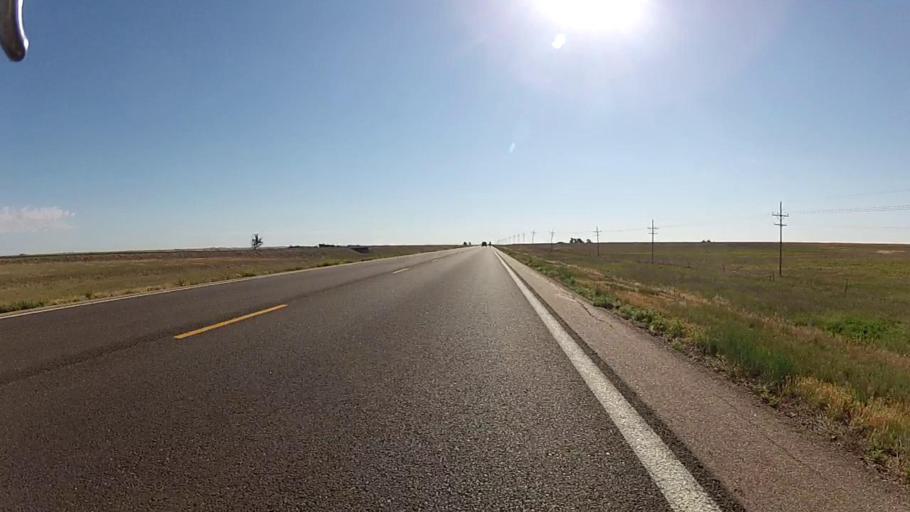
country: US
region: Kansas
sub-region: Haskell County
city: Sublette
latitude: 37.5484
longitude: -100.6091
